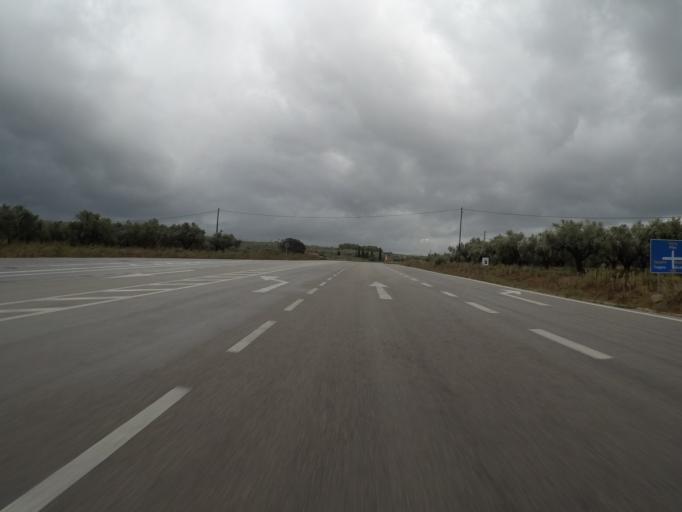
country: GR
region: Peloponnese
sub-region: Nomos Messinias
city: Gargalianoi
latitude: 37.0112
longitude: 21.6548
